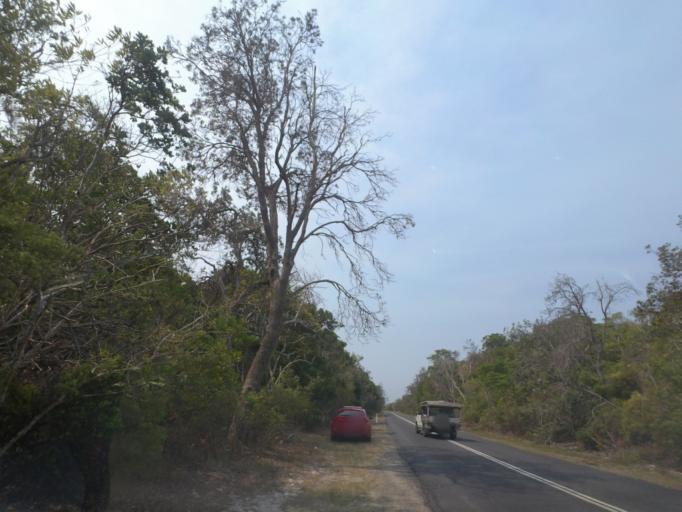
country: AU
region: New South Wales
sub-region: Tweed
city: Pottsville Beach
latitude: -28.4368
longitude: 153.5558
